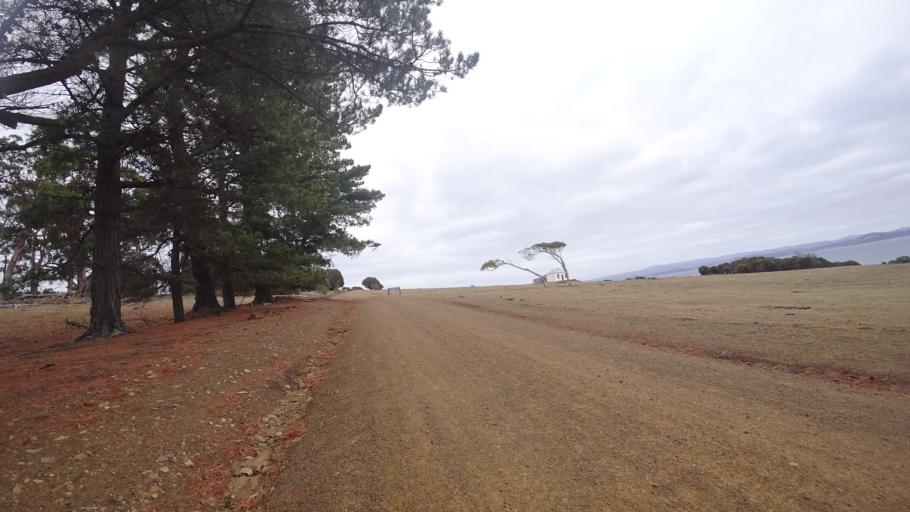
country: AU
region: Tasmania
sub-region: Sorell
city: Sorell
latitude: -42.5835
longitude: 148.0606
